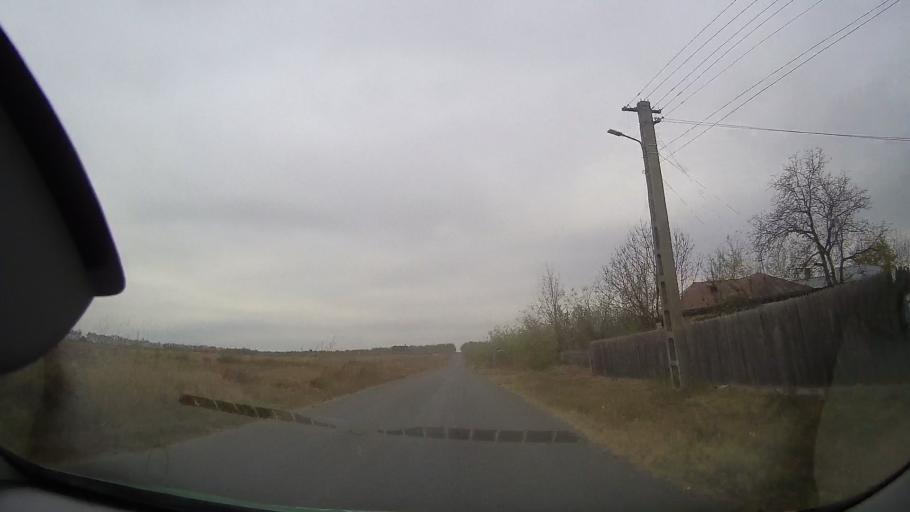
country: RO
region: Buzau
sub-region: Comuna Largu
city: Largu
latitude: 44.9719
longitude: 27.1767
